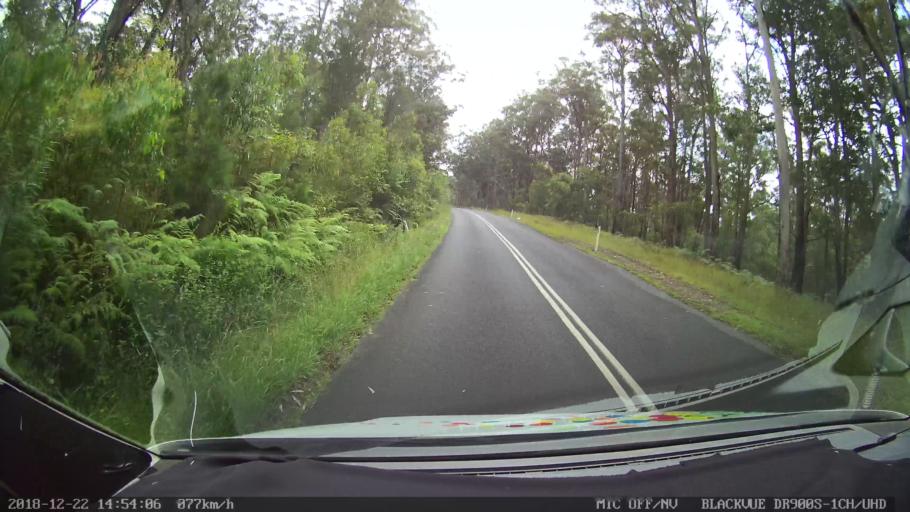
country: AU
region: New South Wales
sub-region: Bellingen
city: Dorrigo
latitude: -30.2240
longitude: 152.5359
